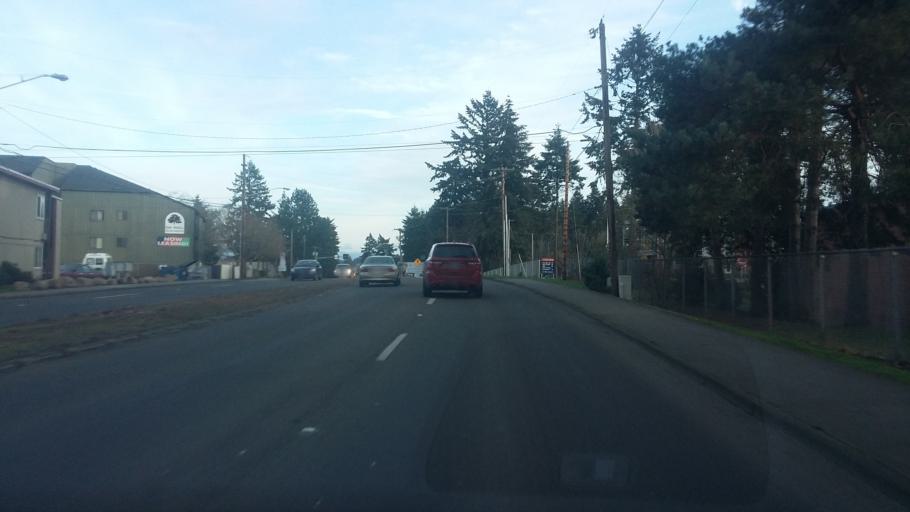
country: US
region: Washington
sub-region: Clark County
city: Vancouver
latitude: 45.6389
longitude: -122.6533
